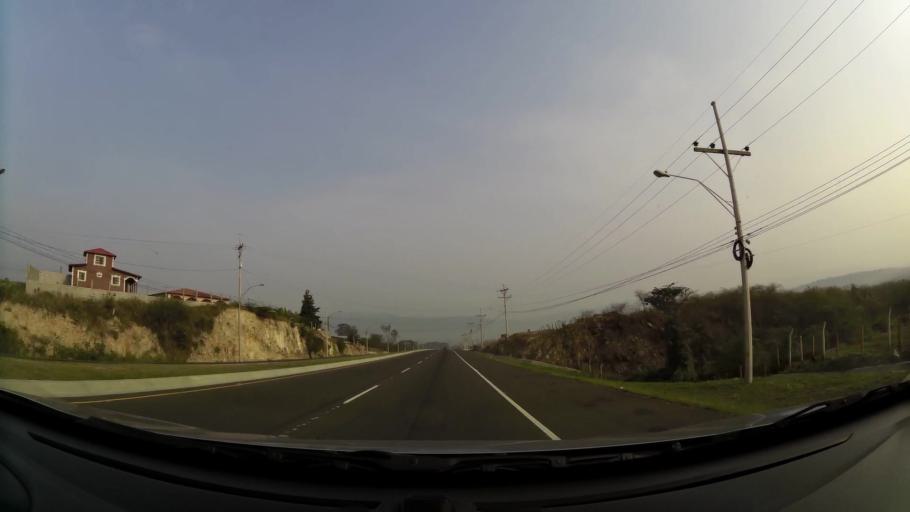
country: HN
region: Francisco Morazan
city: Tamara
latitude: 14.2043
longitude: -87.3480
